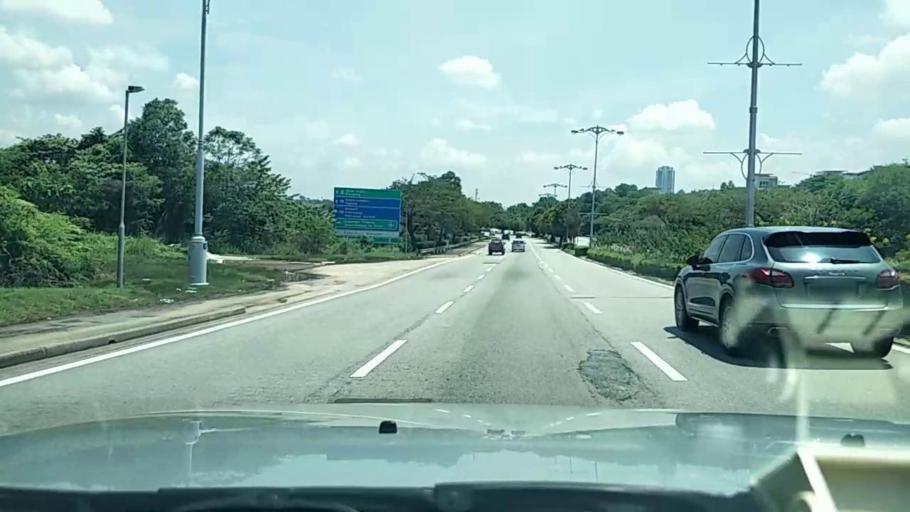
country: MY
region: Putrajaya
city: Putrajaya
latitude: 2.9457
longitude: 101.6710
